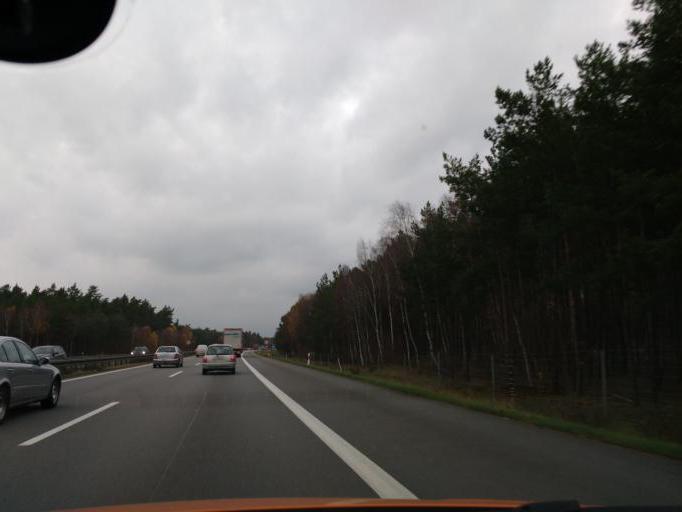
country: DE
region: Brandenburg
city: Wittstock
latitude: 53.1089
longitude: 12.4757
